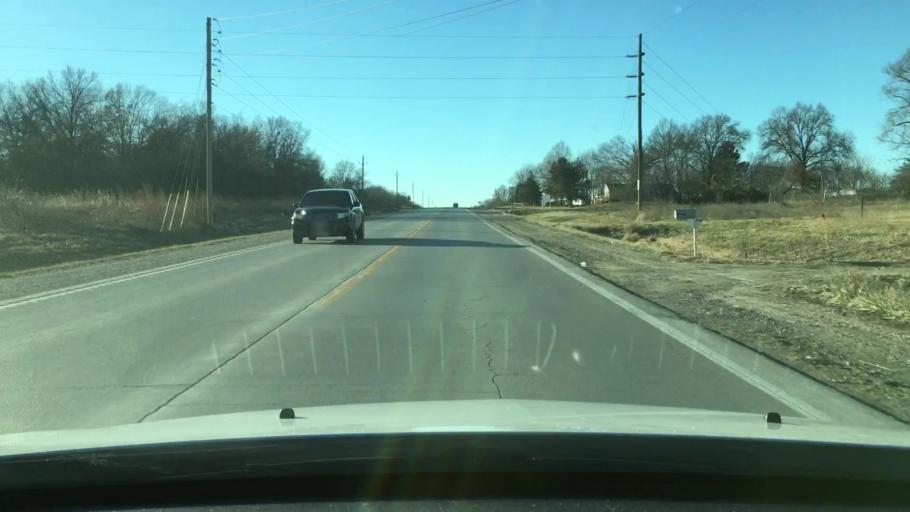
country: US
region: Missouri
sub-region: Audrain County
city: Mexico
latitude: 39.1859
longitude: -91.9390
